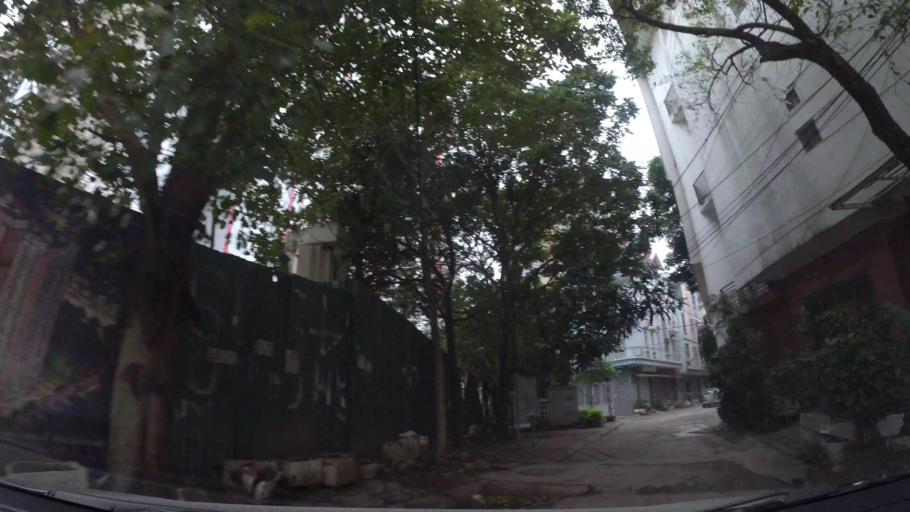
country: VN
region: Ha Noi
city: Cau Dien
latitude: 21.0329
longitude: 105.7821
